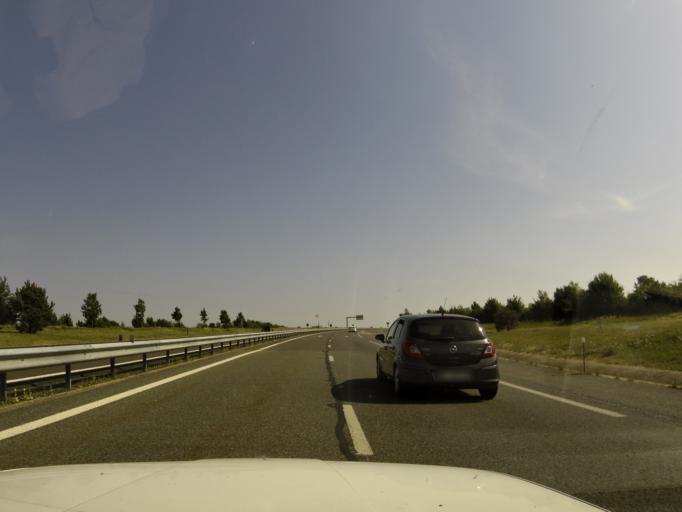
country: FR
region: Midi-Pyrenees
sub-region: Departement de l'Aveyron
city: Severac-le-Chateau
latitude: 44.3072
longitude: 3.1034
